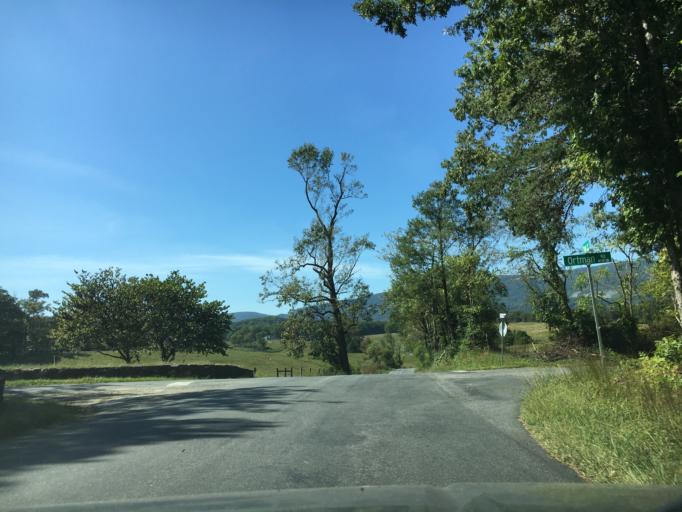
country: US
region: Virginia
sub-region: Albemarle County
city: Crozet
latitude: 38.0175
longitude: -78.7680
